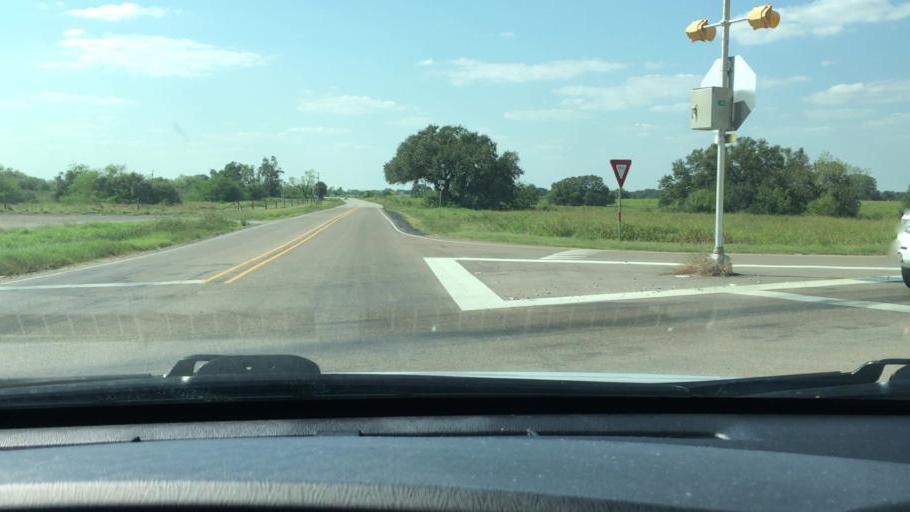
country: US
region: Texas
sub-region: DeWitt County
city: Yorktown
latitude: 28.9200
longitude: -97.3463
